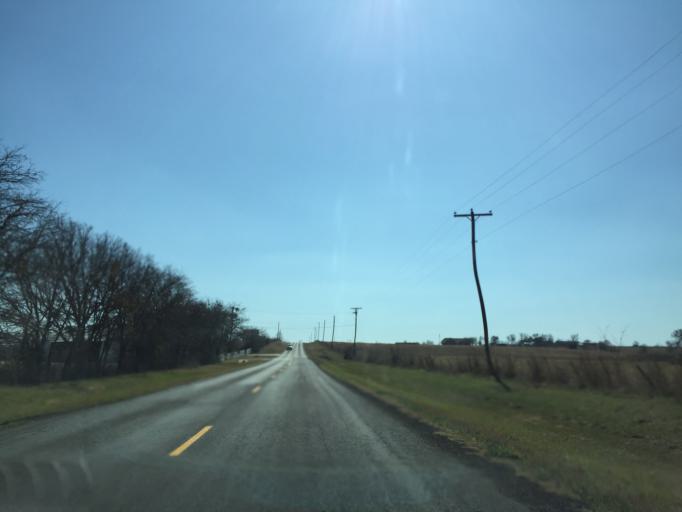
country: US
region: Texas
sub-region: Williamson County
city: Serenada
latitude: 30.7265
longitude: -97.5839
